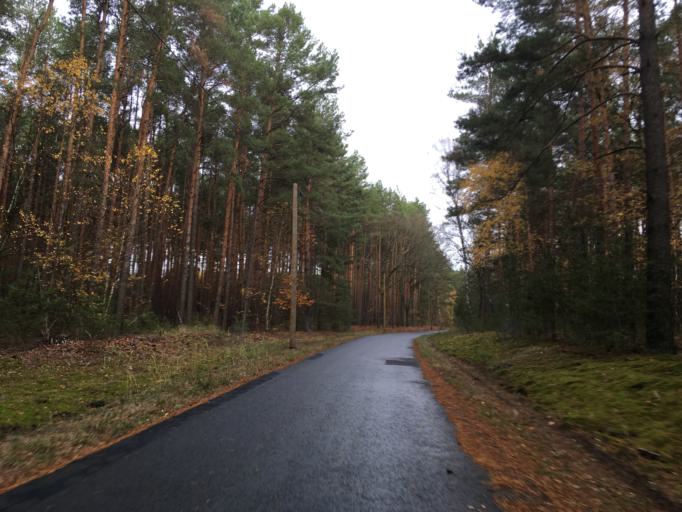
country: DE
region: Brandenburg
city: Tauer
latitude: 51.9139
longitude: 14.4651
